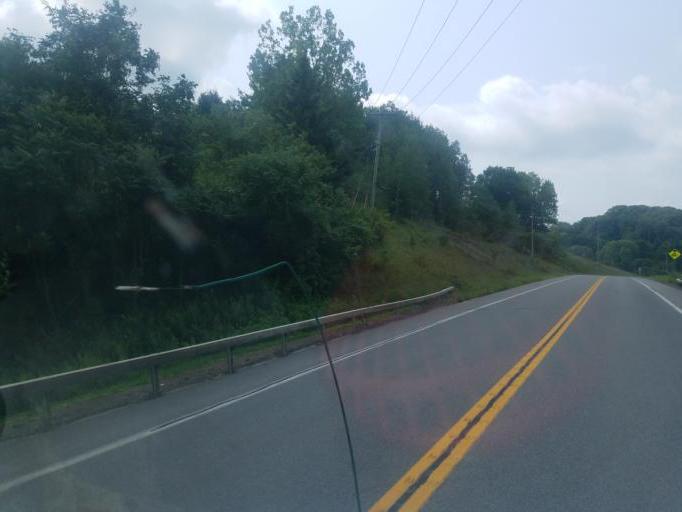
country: US
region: New York
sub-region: Herkimer County
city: Herkimer
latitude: 43.0135
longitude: -74.9408
